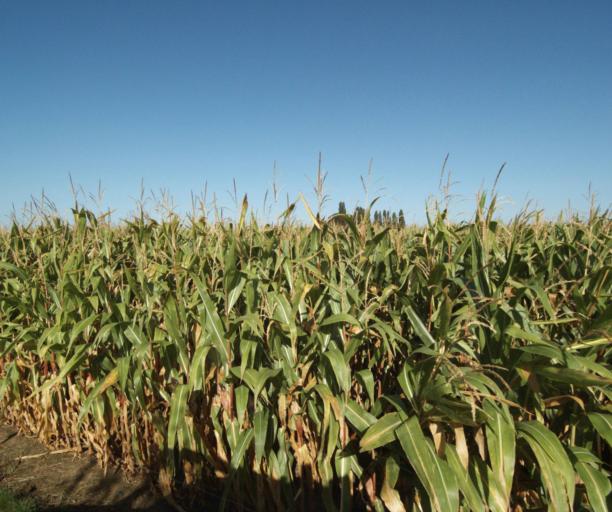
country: FR
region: Nord-Pas-de-Calais
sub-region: Departement du Nord
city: Sailly-lez-Lannoy
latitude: 50.6485
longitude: 3.2179
